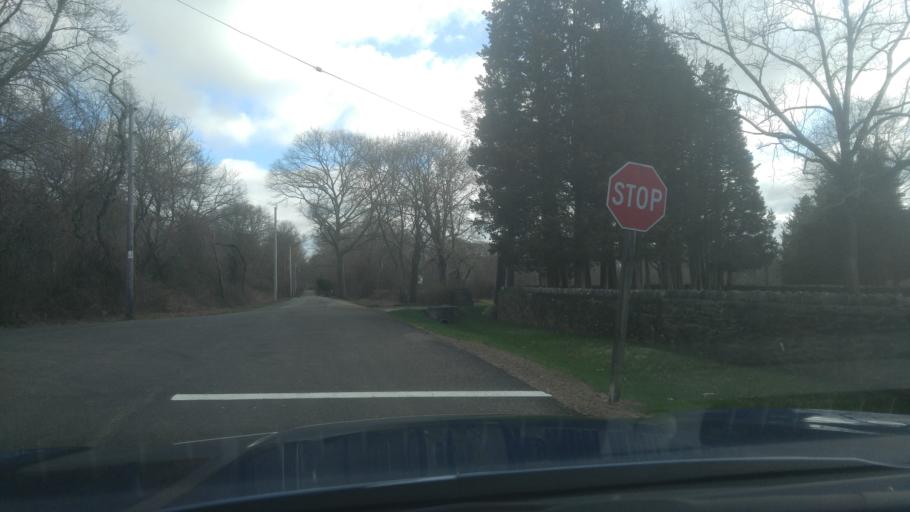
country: US
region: Rhode Island
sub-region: Newport County
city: Jamestown
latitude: 41.5714
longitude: -71.3722
